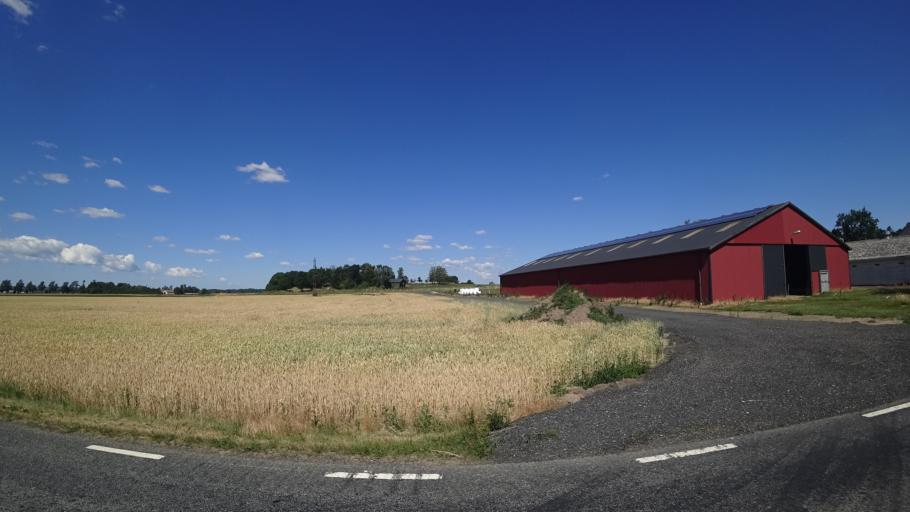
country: SE
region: Skane
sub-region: Kristianstads Kommun
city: Onnestad
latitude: 56.0726
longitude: 14.0754
